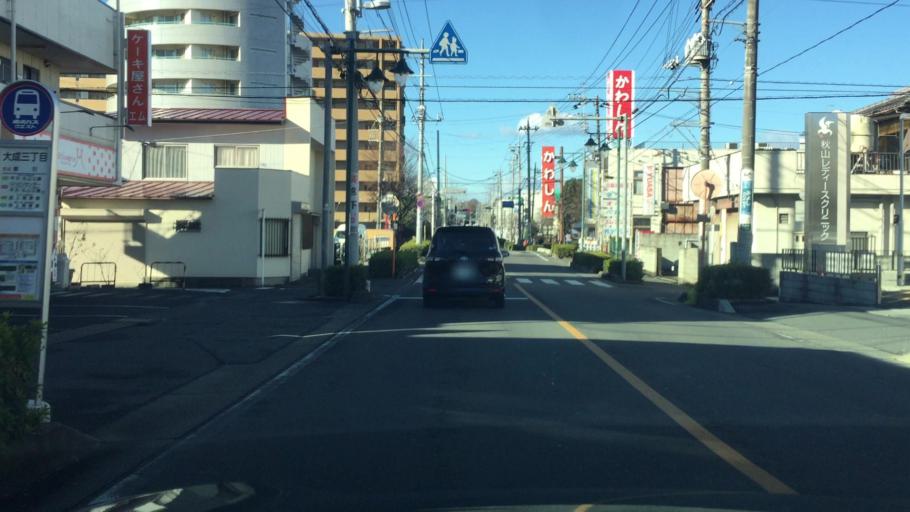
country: JP
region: Saitama
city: Yono
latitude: 35.9186
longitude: 139.6123
